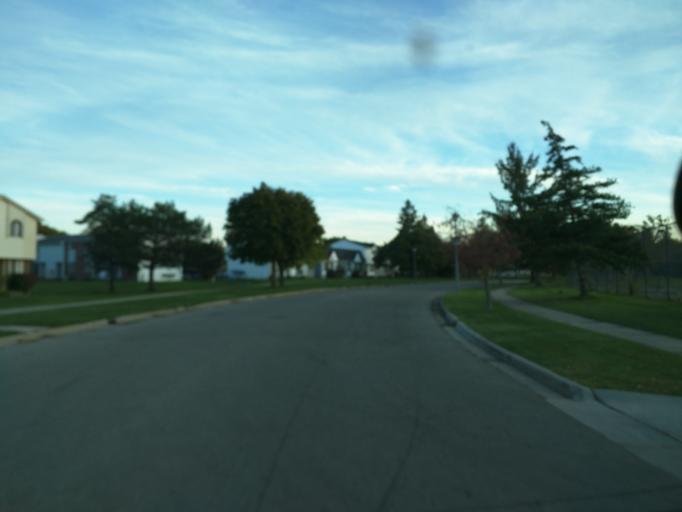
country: US
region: Michigan
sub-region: Eaton County
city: Waverly
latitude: 42.6879
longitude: -84.6061
